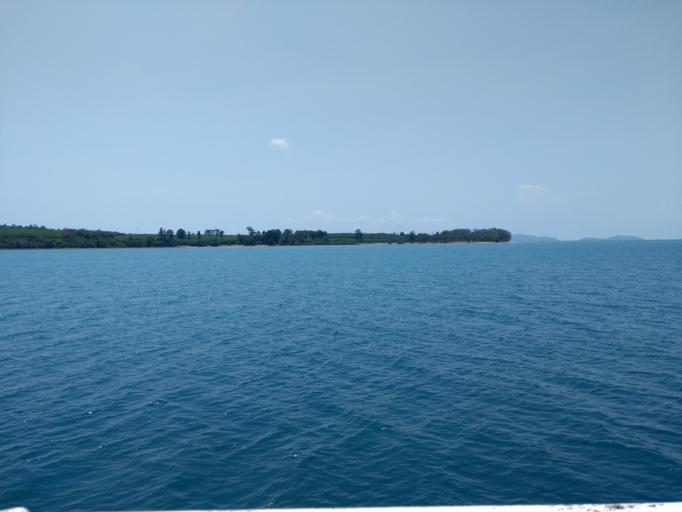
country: TH
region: Trat
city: Ko Kut
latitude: 11.8119
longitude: 102.5160
